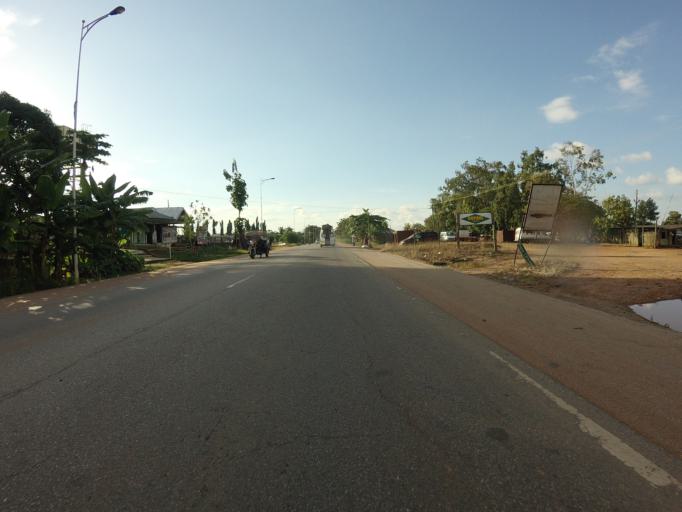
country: GH
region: Ashanti
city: Tafo
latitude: 6.9236
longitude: -1.6621
